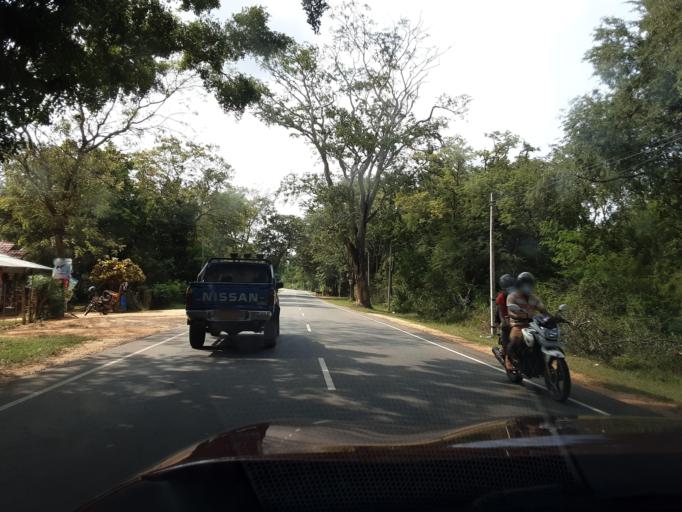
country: LK
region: Uva
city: Haputale
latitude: 6.3646
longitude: 81.1780
